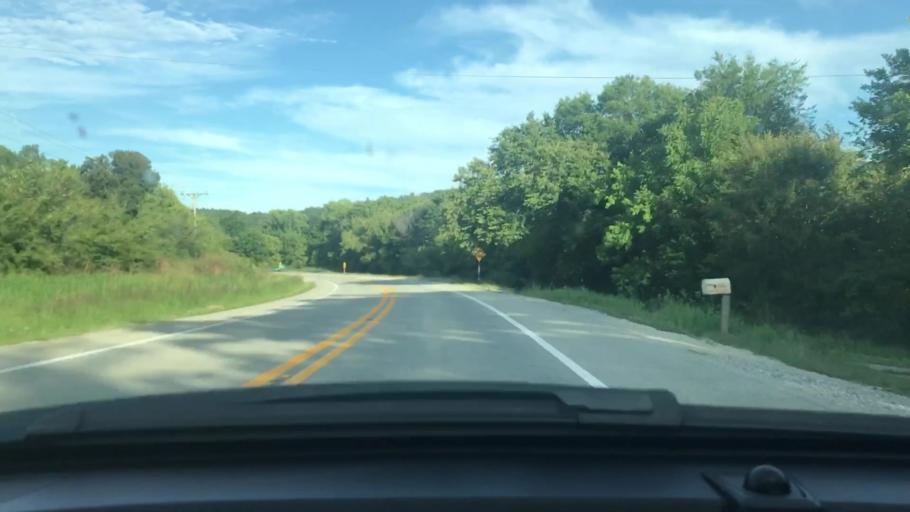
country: US
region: Arkansas
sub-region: Sharp County
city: Cherokee Village
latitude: 36.2732
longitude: -91.3355
